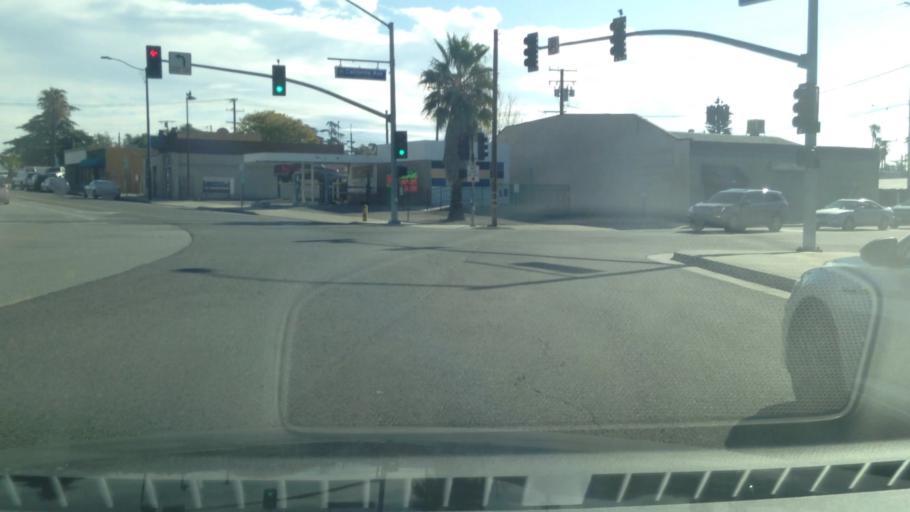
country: US
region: California
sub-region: Riverside County
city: Beaumont
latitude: 33.9295
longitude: -116.9817
